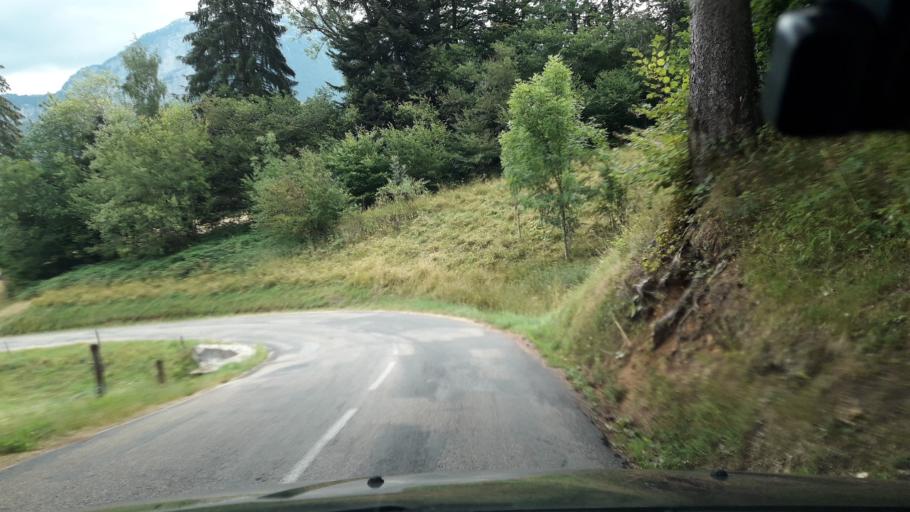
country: FR
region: Rhone-Alpes
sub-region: Departement de la Savoie
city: Vimines
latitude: 45.4463
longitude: 5.8699
